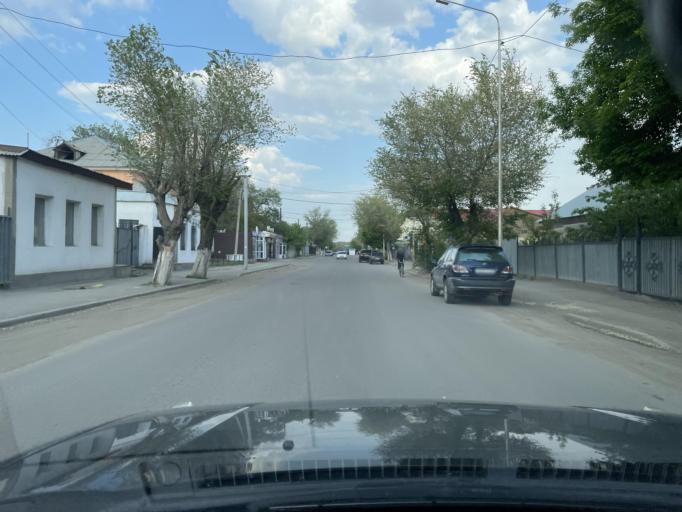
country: KZ
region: Qaraghandy
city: Zhezqazghan
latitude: 47.7941
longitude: 67.7106
